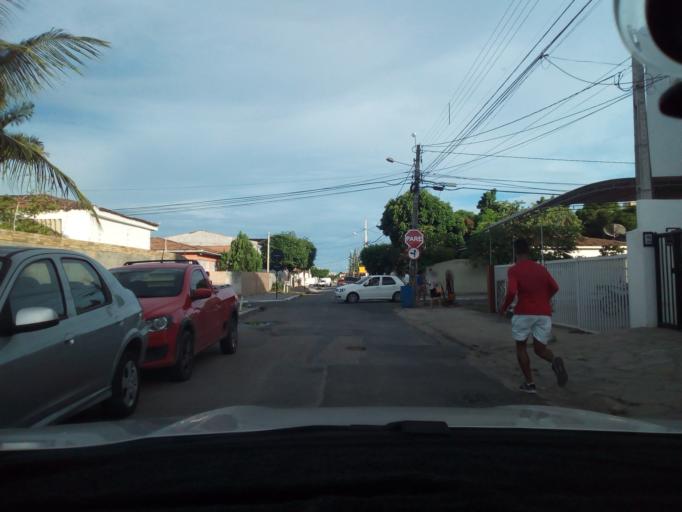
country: BR
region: Paraiba
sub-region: Joao Pessoa
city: Joao Pessoa
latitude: -7.1725
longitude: -34.8586
